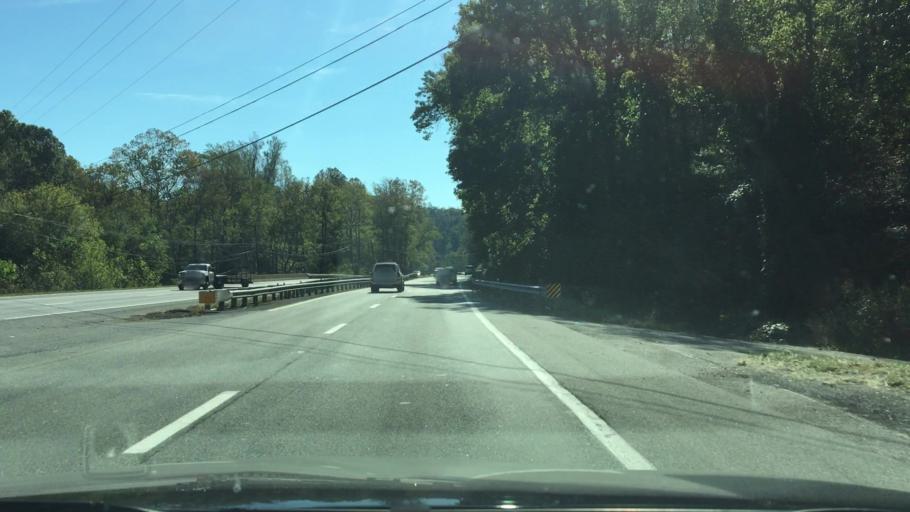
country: US
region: Virginia
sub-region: Roanoke County
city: Narrows
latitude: 37.1262
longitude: -79.9605
